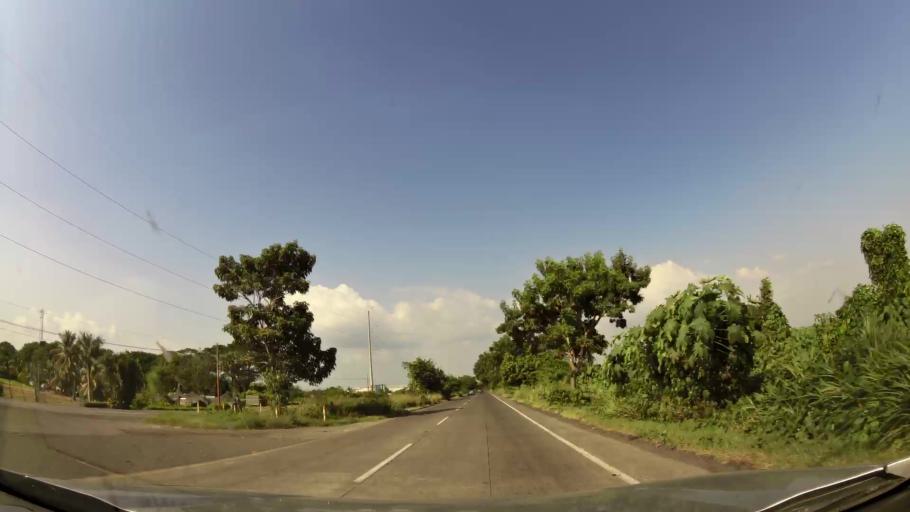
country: GT
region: Escuintla
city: Puerto San Jose
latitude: 13.9726
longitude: -90.7885
